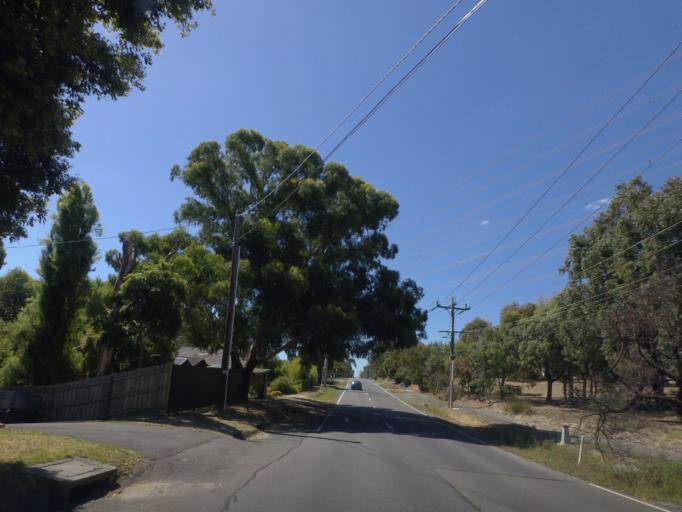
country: AU
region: Victoria
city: Mitcham
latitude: -37.8044
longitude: 145.2149
